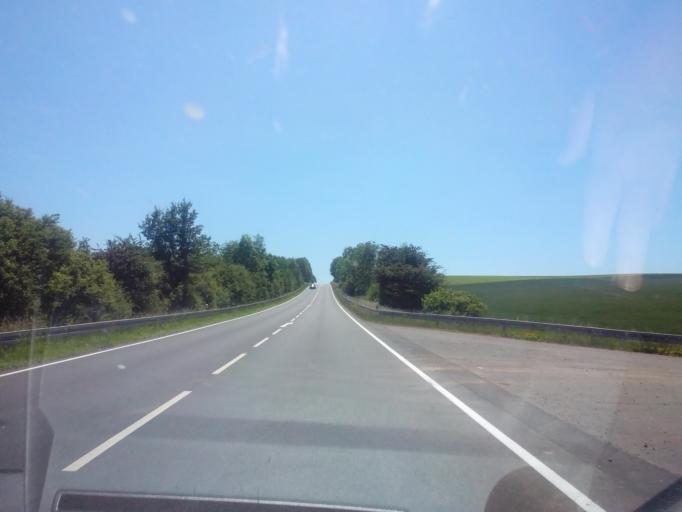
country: DE
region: Rheinland-Pfalz
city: Kirf
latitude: 49.5239
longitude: 6.4599
